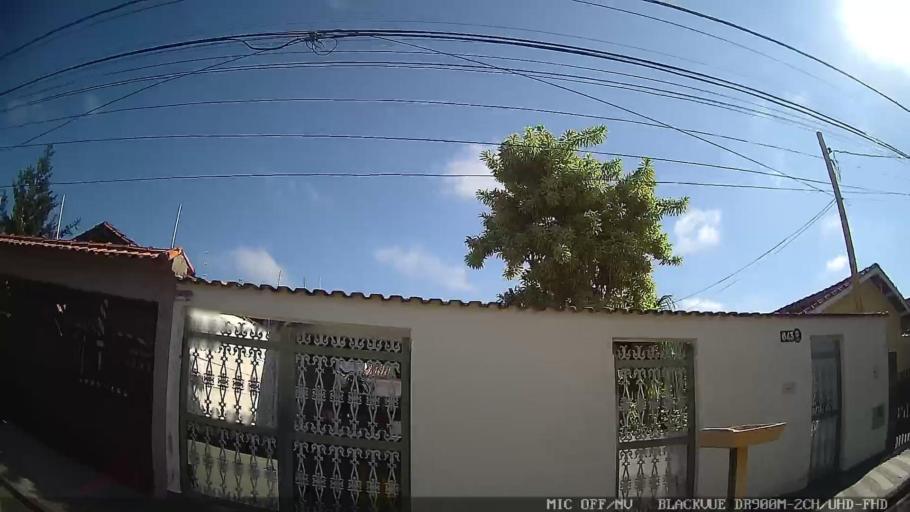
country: BR
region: Sao Paulo
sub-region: Peruibe
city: Peruibe
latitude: -24.2841
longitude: -46.9575
